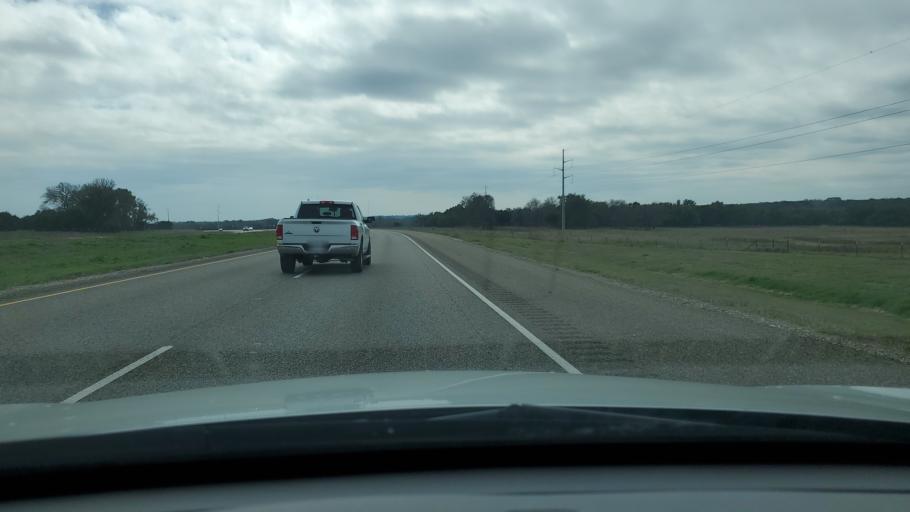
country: US
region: Texas
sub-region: Williamson County
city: Florence
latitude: 30.7744
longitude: -97.7593
